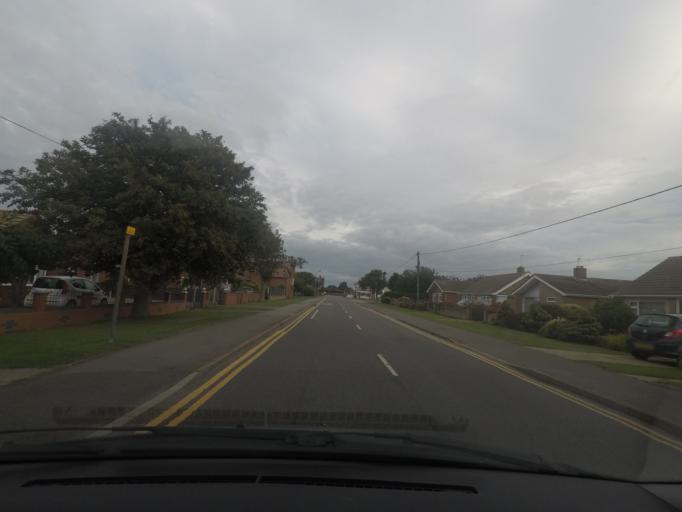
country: GB
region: England
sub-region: Lincolnshire
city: Chapel Saint Leonards
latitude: 53.2250
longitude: 0.3365
